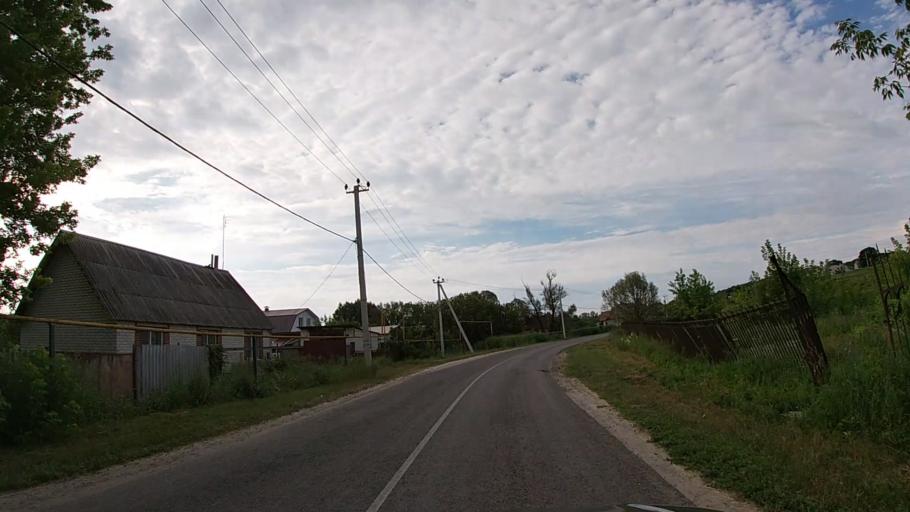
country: RU
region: Belgorod
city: Severnyy
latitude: 50.7083
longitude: 36.6002
